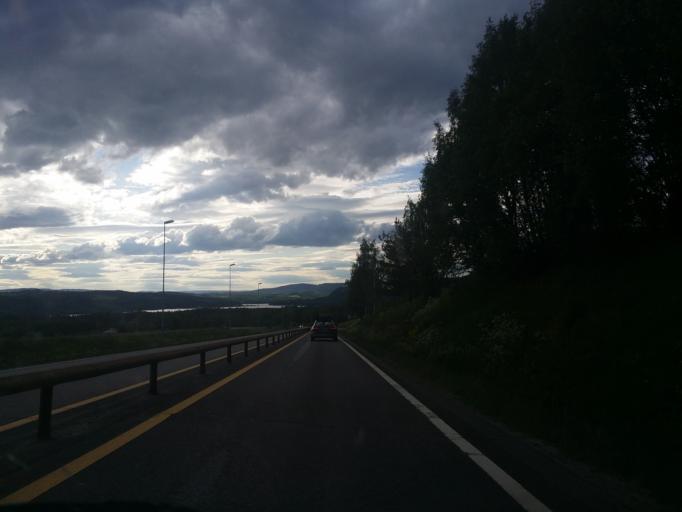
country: NO
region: Hedmark
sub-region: Ringsaker
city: Brumunddal
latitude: 60.8573
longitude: 10.9774
